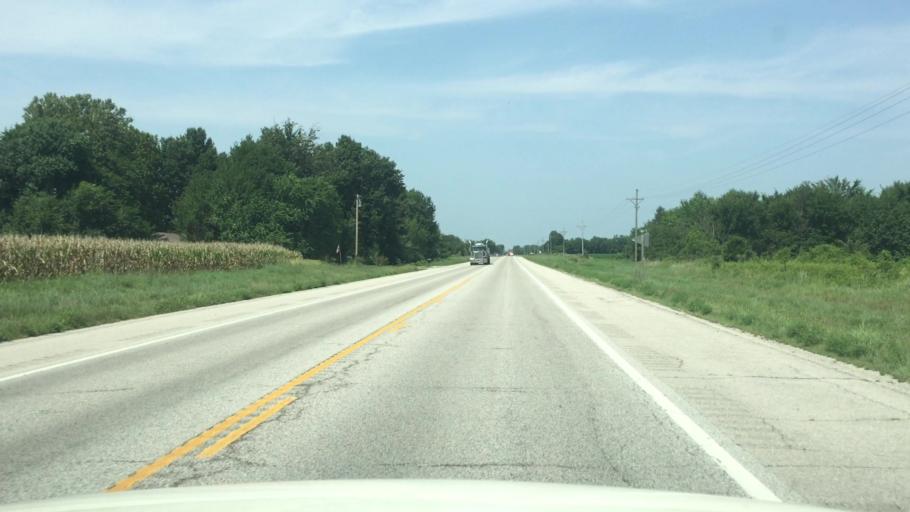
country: US
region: Kansas
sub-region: Cherokee County
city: Galena
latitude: 37.1513
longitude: -94.7043
